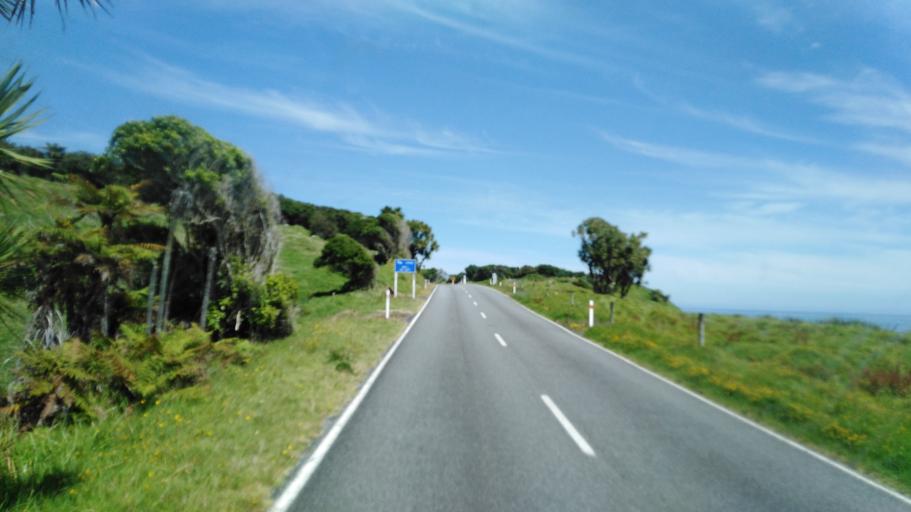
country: NZ
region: West Coast
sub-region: Buller District
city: Westport
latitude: -41.5897
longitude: 171.8919
